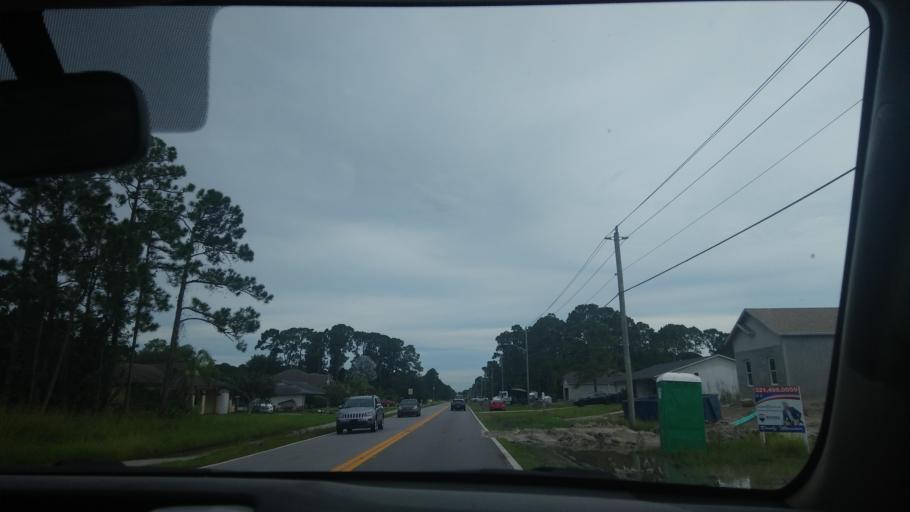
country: US
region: Florida
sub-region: Brevard County
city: Grant-Valkaria
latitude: 27.9750
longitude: -80.6347
